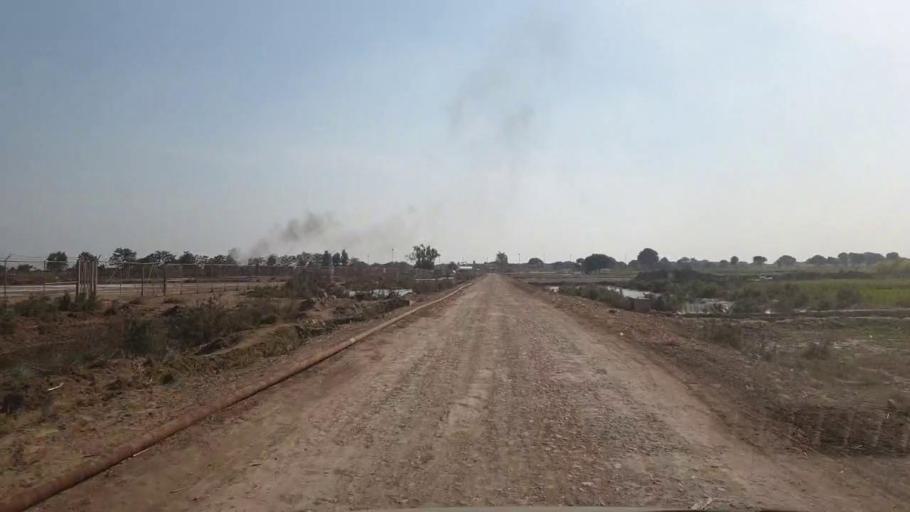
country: PK
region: Sindh
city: Chambar
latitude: 25.3295
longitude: 68.7738
